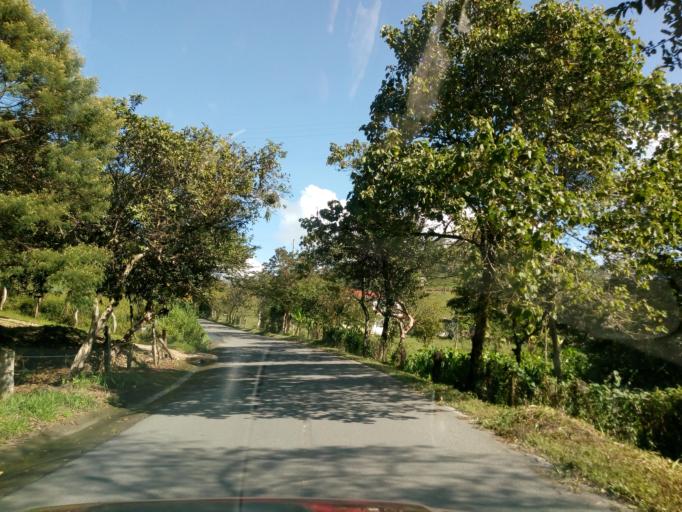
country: CO
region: Boyaca
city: Moniquira
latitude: 5.8680
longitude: -73.5526
